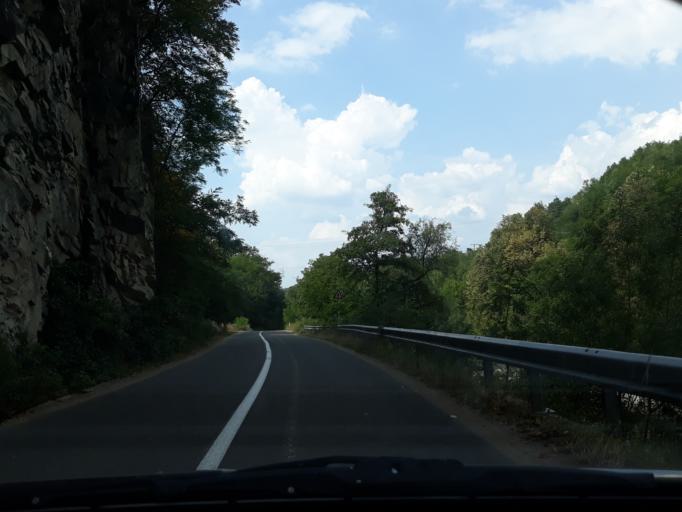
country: RO
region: Bihor
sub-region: Comuna Pietroasa
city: Pietroasa
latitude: 46.5881
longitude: 22.5645
